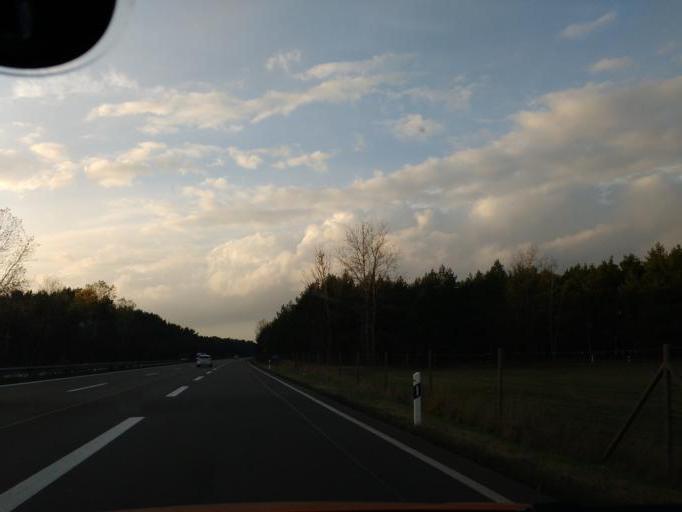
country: DE
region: Mecklenburg-Vorpommern
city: Neustadt-Glewe
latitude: 53.3710
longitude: 11.6497
